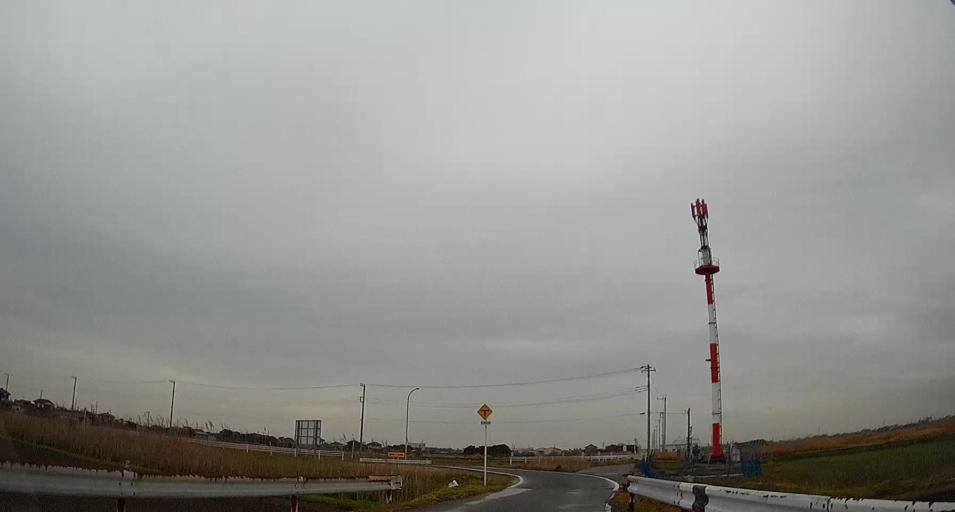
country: JP
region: Chiba
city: Kisarazu
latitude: 35.4246
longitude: 139.9095
